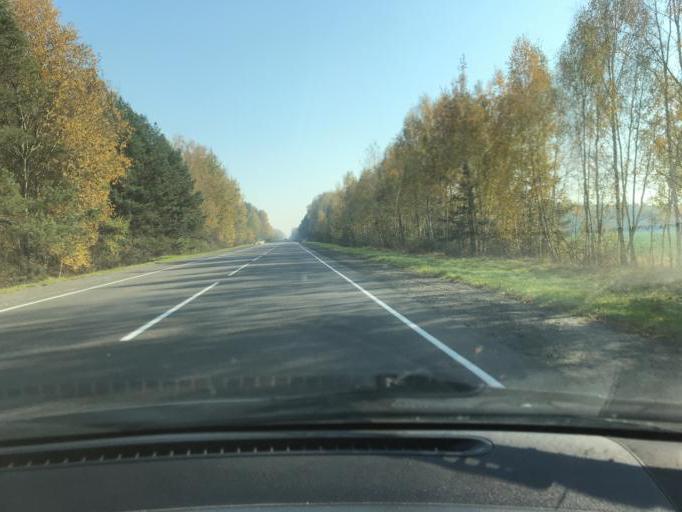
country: BY
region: Brest
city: Horad Luninyets
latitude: 52.3022
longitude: 26.7138
